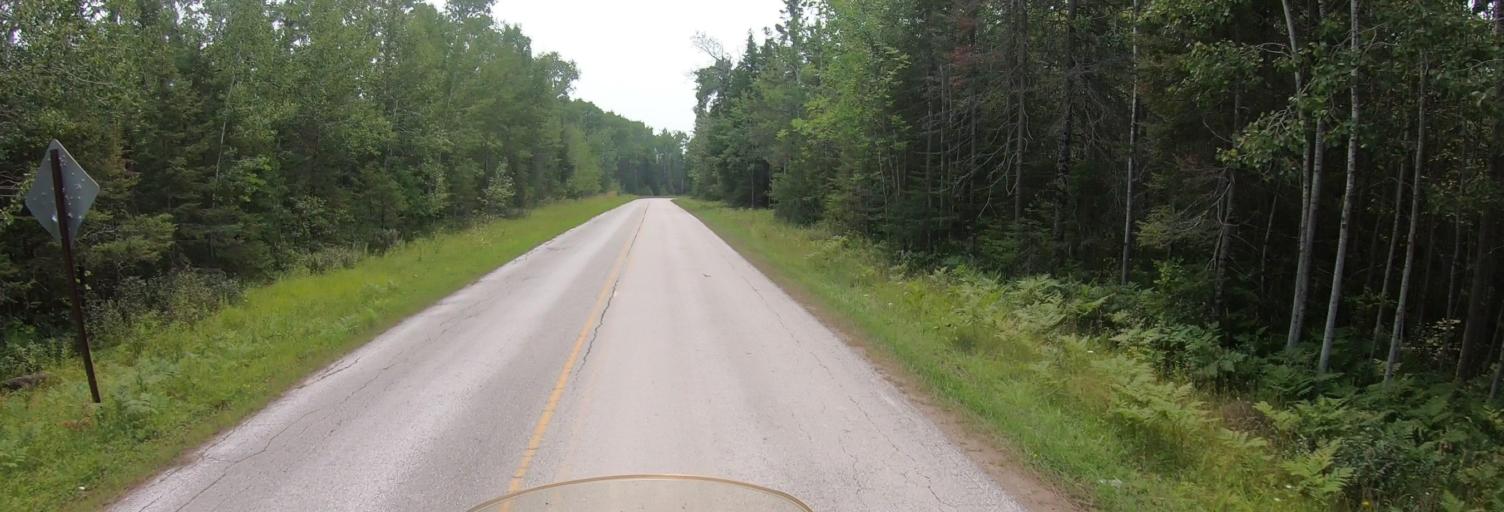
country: CA
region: Ontario
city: Thessalon
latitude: 46.0659
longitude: -83.6648
